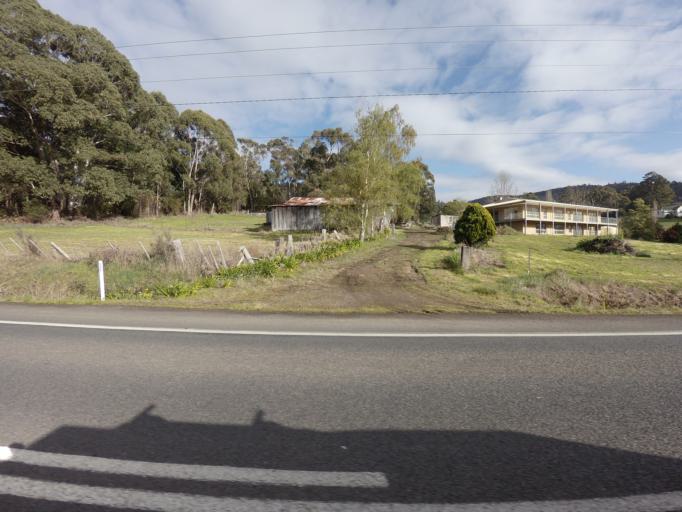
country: AU
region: Tasmania
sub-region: Huon Valley
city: Franklin
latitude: -43.0614
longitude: 147.0278
